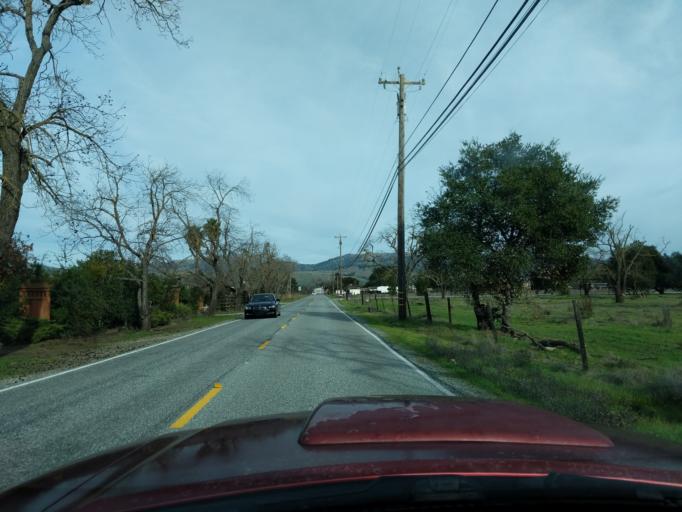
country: US
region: California
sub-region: Santa Clara County
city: San Martin
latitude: 37.0909
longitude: -121.6193
